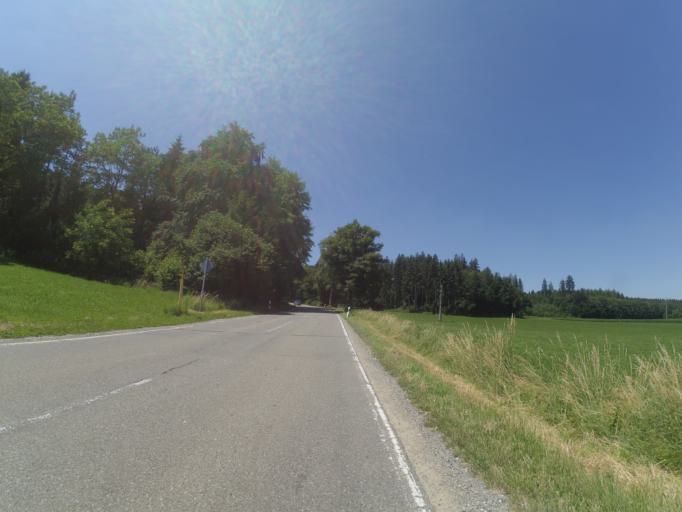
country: DE
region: Baden-Wuerttemberg
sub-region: Tuebingen Region
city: Bad Waldsee
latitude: 47.9005
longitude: 9.7857
